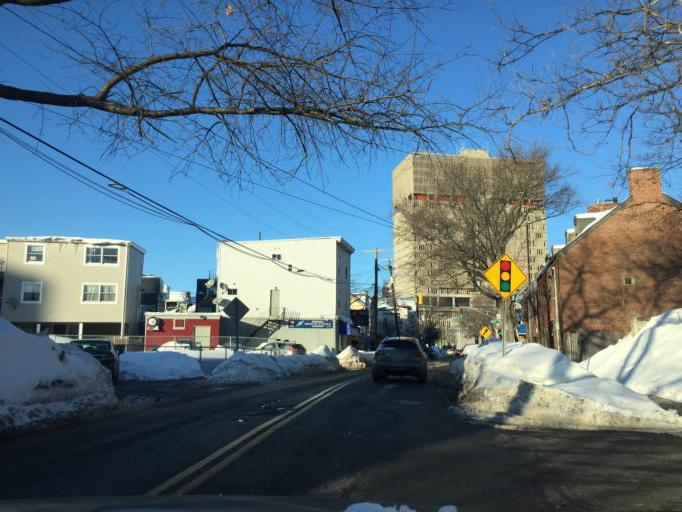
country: US
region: Massachusetts
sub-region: Suffolk County
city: Boston
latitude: 42.3672
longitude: -71.0816
